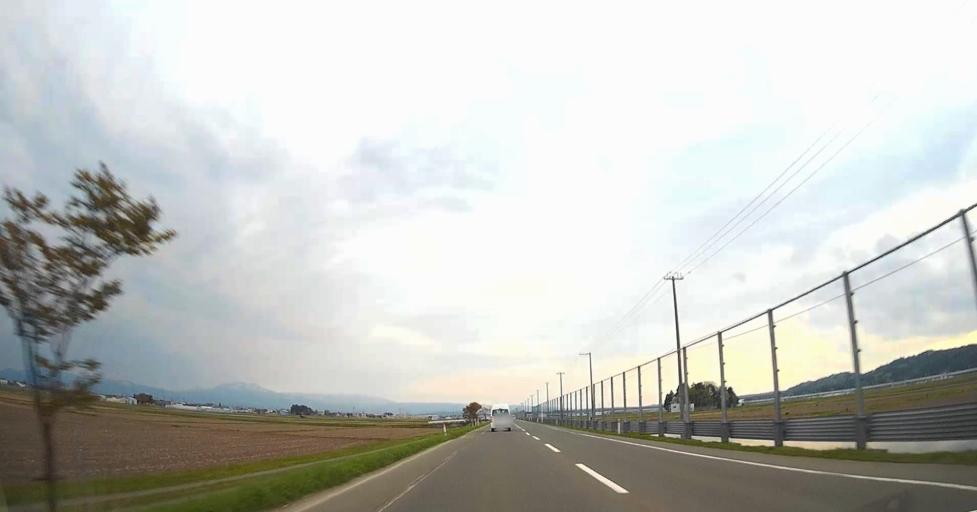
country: JP
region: Aomori
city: Aomori Shi
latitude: 40.8959
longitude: 140.6679
